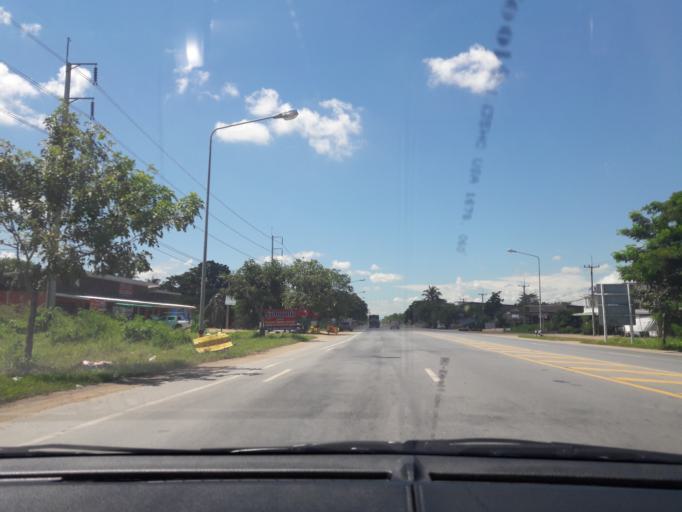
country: TH
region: Kanchanaburi
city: Tha Maka
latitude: 14.0428
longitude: 99.7865
